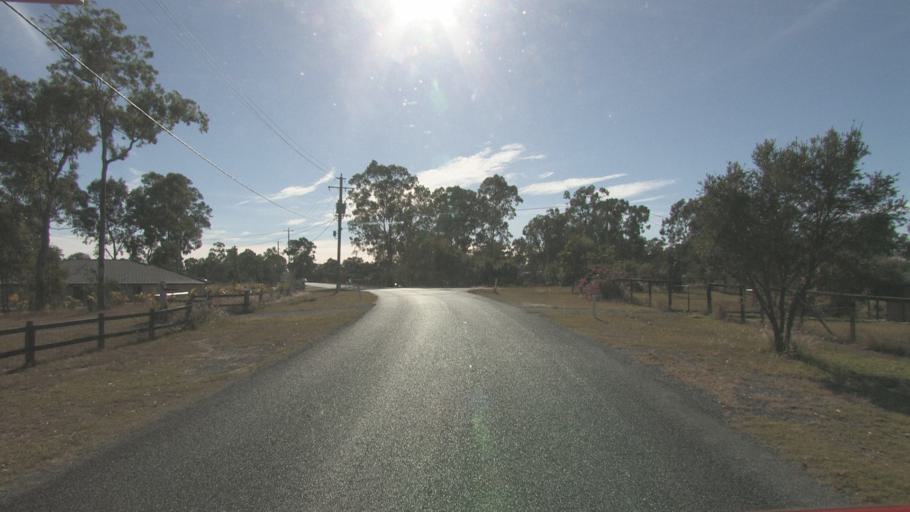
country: AU
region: Queensland
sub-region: Ipswich
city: Springfield Lakes
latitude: -27.6975
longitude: 152.9316
